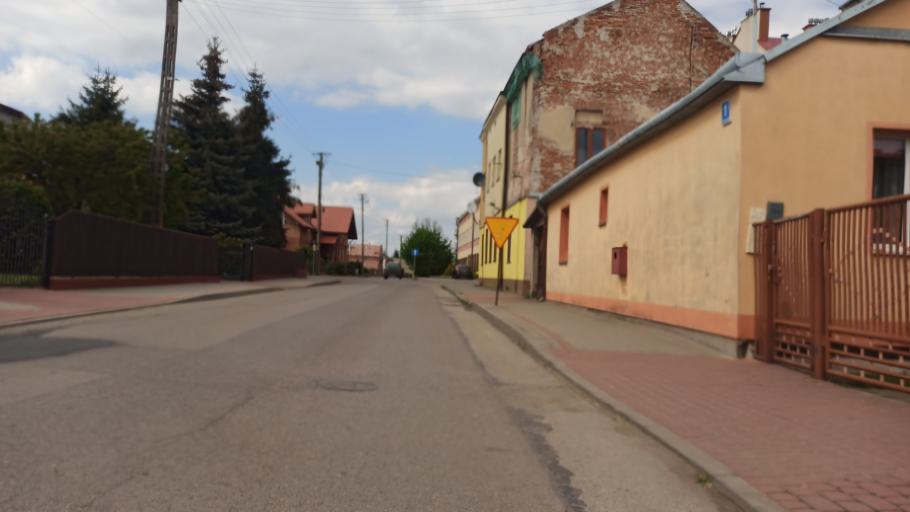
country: PL
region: Subcarpathian Voivodeship
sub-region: Powiat jaroslawski
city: Radymno
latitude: 49.9514
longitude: 22.8157
